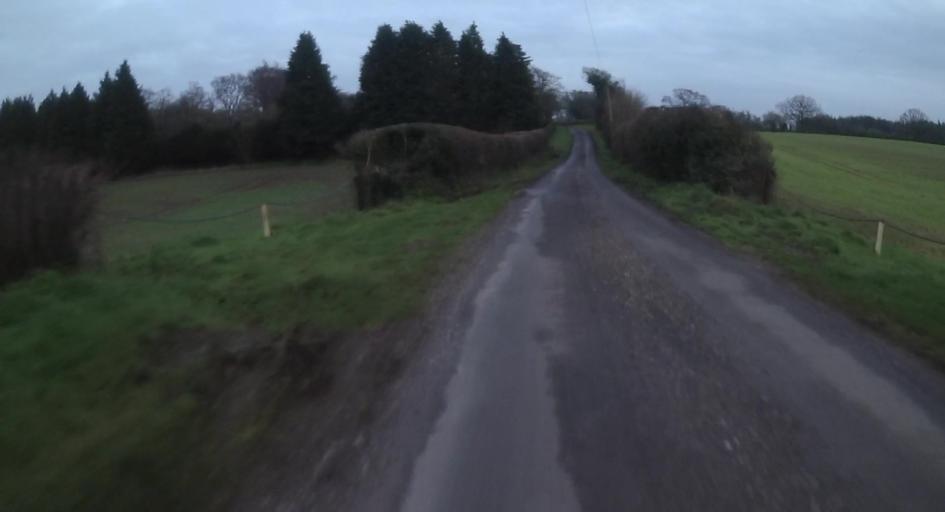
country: GB
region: England
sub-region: Hampshire
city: Overton
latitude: 51.2589
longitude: -1.3084
